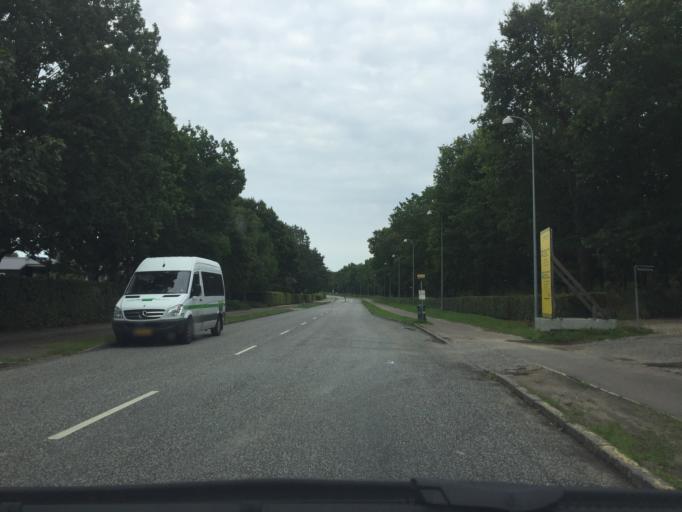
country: DK
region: Capital Region
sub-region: Lyngby-Tarbaek Kommune
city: Kongens Lyngby
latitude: 55.7873
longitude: 12.5159
